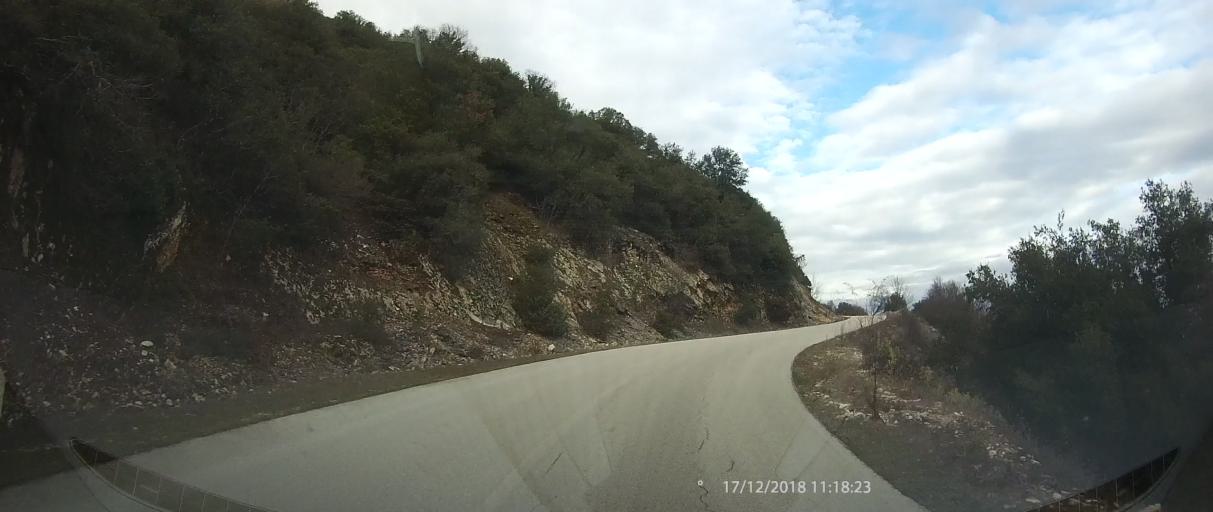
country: GR
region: Epirus
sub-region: Nomos Ioanninon
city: Kalpaki
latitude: 39.9531
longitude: 20.6583
